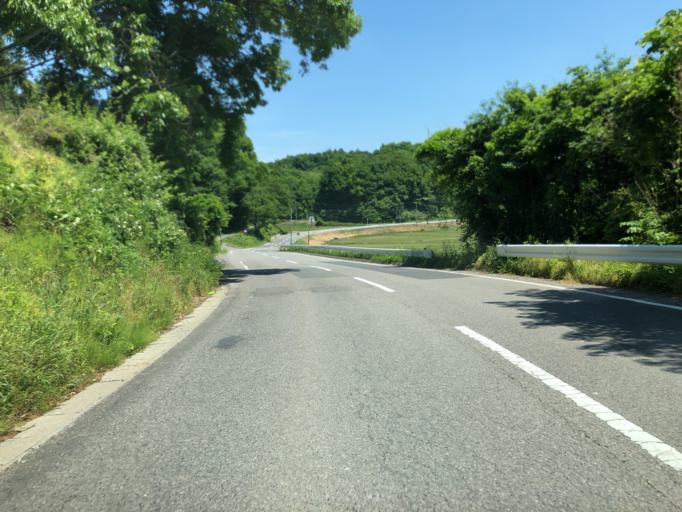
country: JP
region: Fukushima
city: Miharu
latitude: 37.4992
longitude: 140.4805
